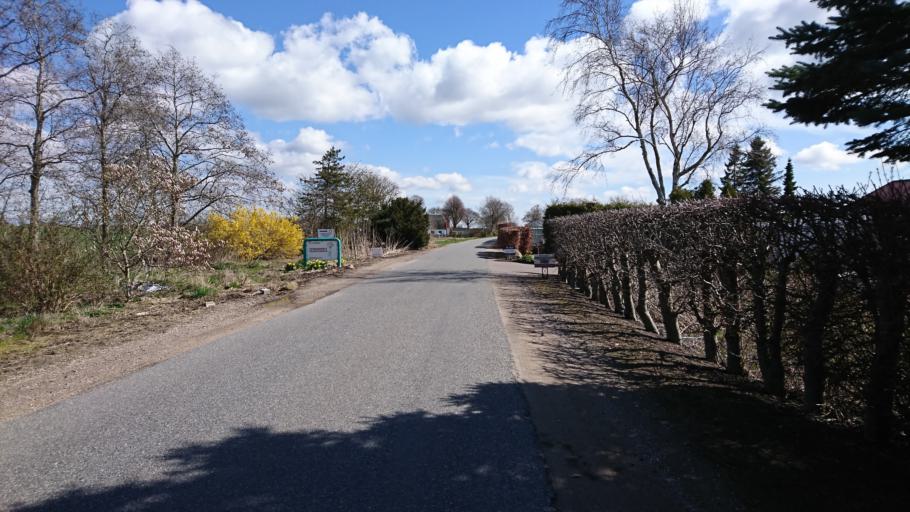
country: DK
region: Capital Region
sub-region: Egedal Kommune
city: Vekso
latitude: 55.7686
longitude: 12.2364
